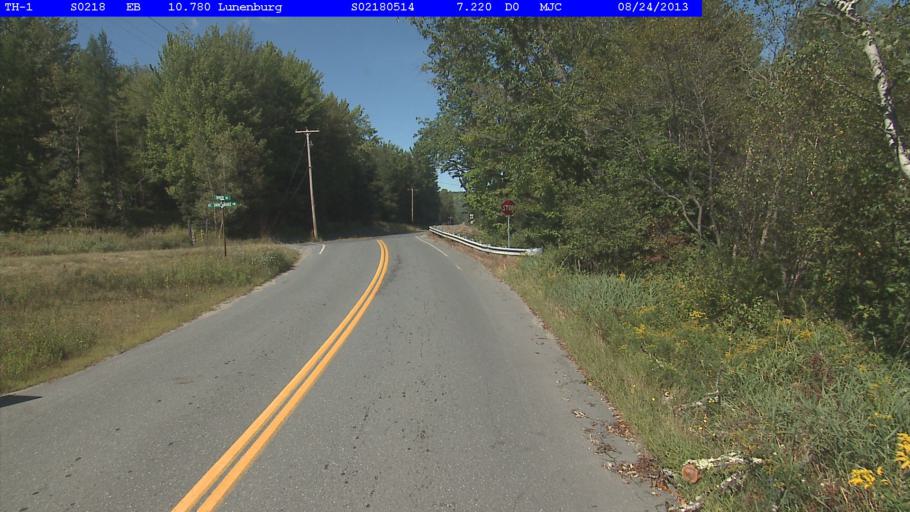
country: US
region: New Hampshire
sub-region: Coos County
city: Lancaster
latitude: 44.4653
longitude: -71.6524
